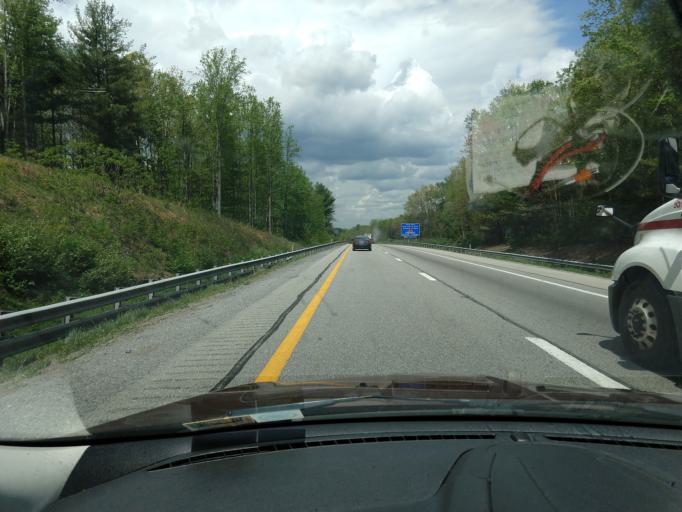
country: US
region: West Virginia
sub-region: Mercer County
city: Athens
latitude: 37.4014
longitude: -81.0609
